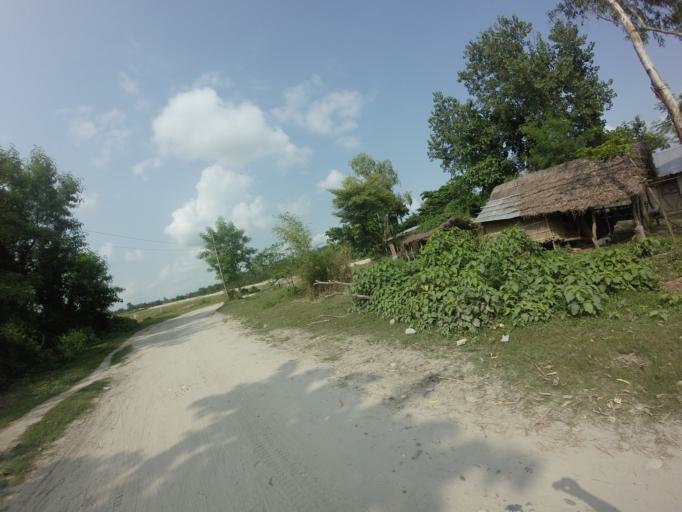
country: NP
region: Far Western
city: Tikapur
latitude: 28.4456
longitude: 81.0746
